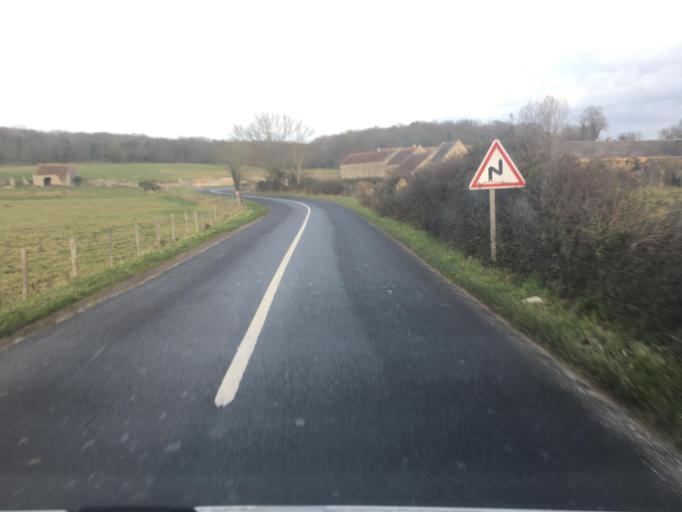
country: FR
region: Lower Normandy
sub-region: Departement du Calvados
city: Creully
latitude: 49.2880
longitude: -0.5411
